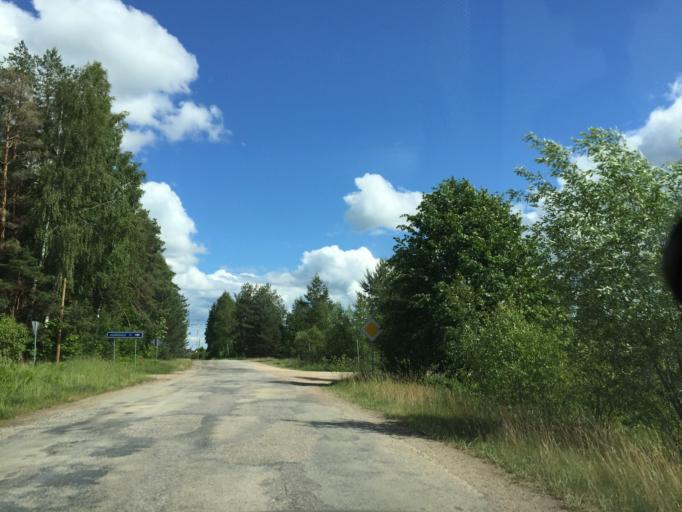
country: LT
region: Panevezys
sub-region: Birzai
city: Birzai
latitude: 56.3855
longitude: 24.6343
